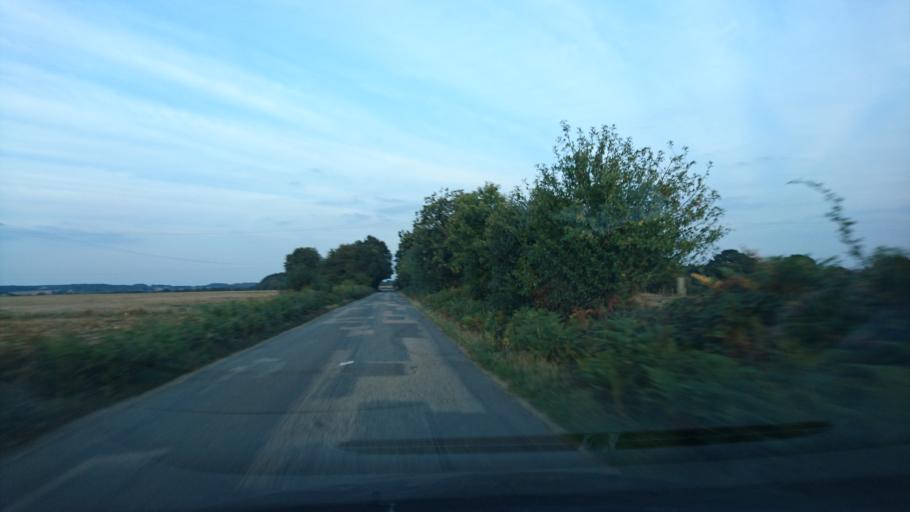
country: FR
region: Brittany
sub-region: Departement du Morbihan
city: Guer
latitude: 47.8837
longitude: -2.0666
